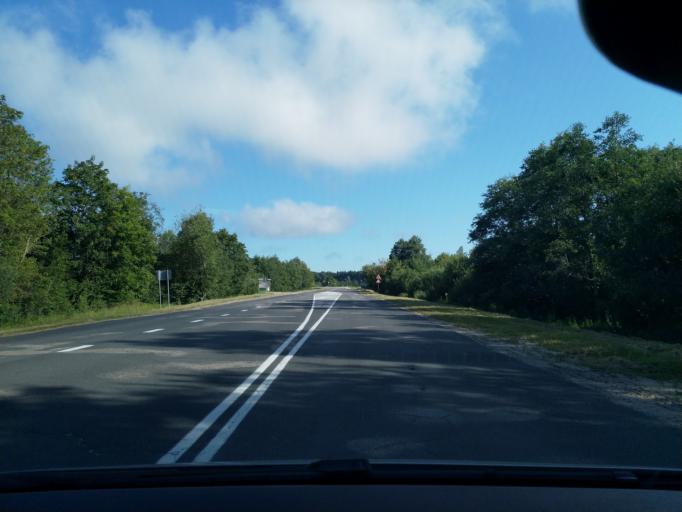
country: LV
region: Kuldigas Rajons
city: Kuldiga
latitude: 56.9638
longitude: 22.0033
